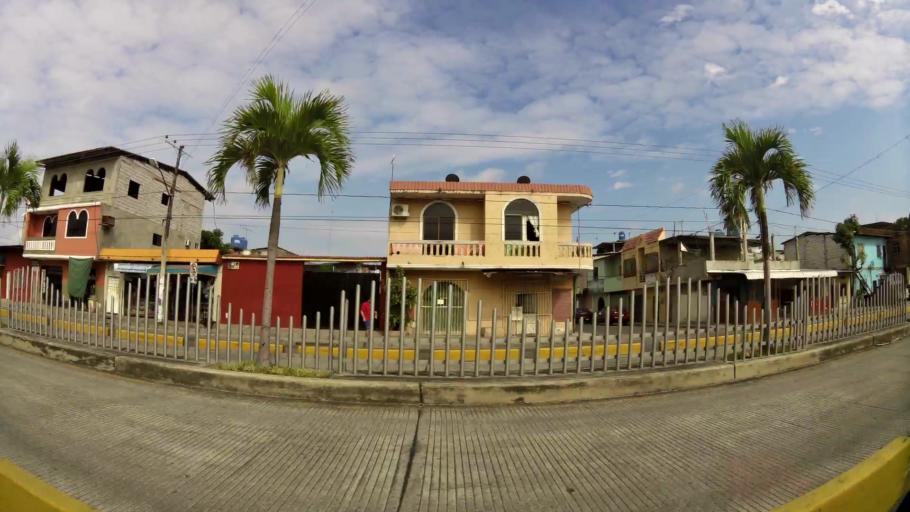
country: EC
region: Guayas
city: Guayaquil
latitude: -2.2572
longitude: -79.8791
